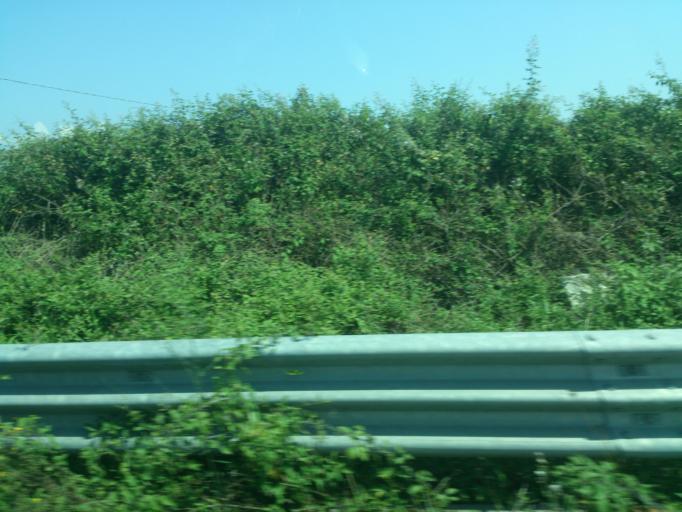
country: IT
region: Calabria
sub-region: Provincia di Reggio Calabria
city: Rosarno
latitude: 38.4668
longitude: 16.0096
